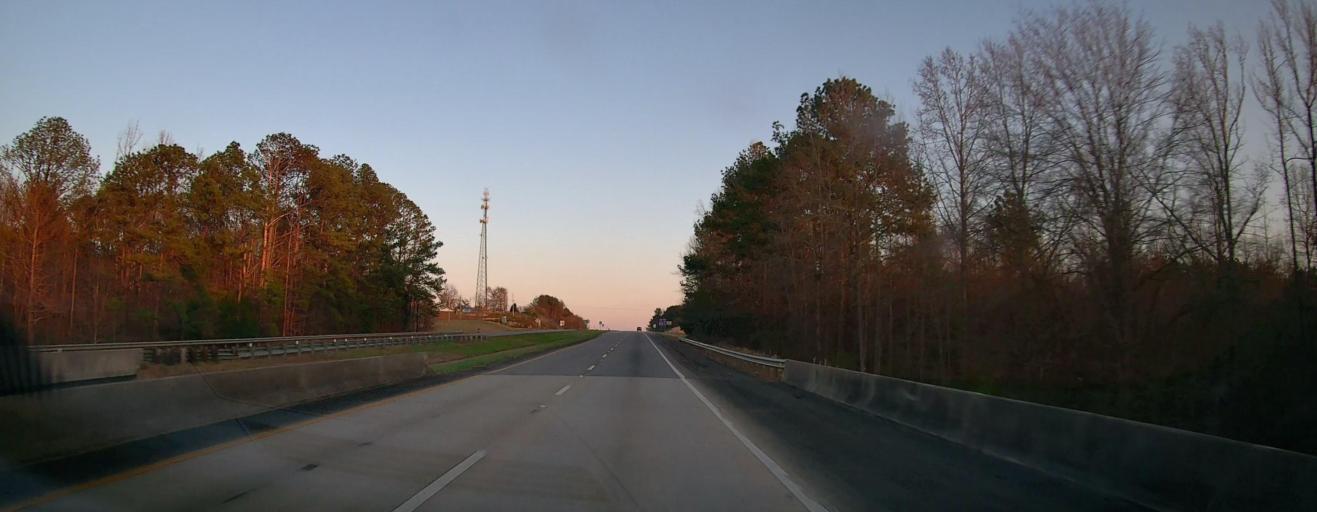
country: US
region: Alabama
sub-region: Coosa County
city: Goodwater
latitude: 32.9991
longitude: -86.0807
